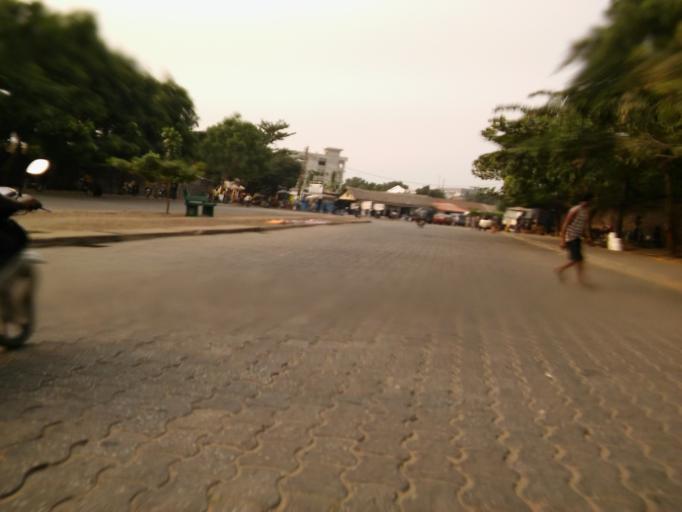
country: BJ
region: Littoral
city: Cotonou
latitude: 6.3573
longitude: 2.4074
